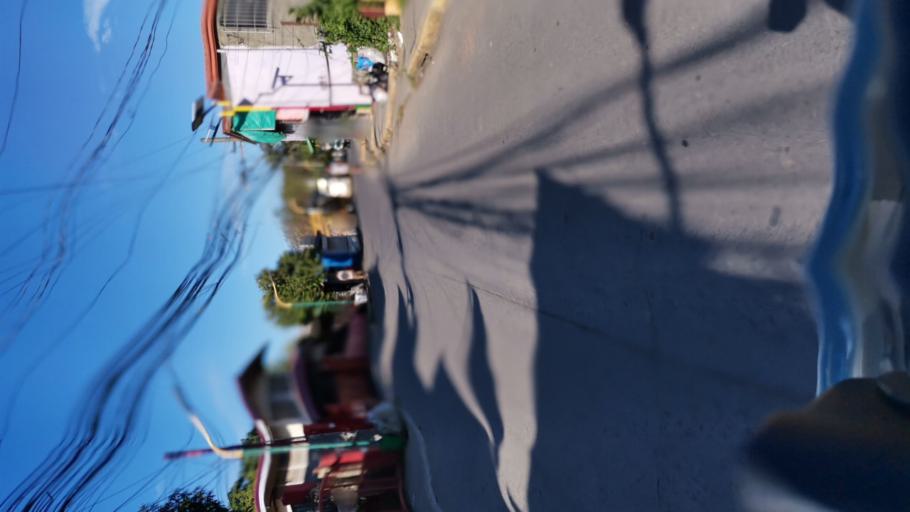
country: PH
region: Calabarzon
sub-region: Province of Batangas
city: Tanauan
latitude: 14.0807
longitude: 121.1461
